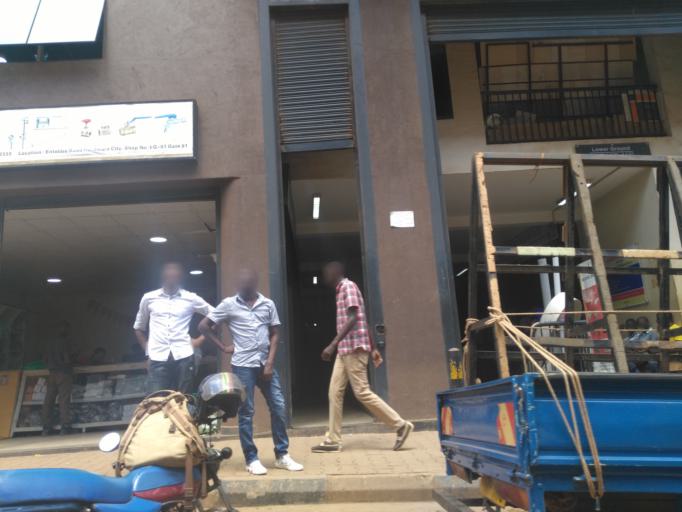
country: UG
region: Central Region
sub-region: Kampala District
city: Kampala
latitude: 0.3105
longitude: 32.5801
